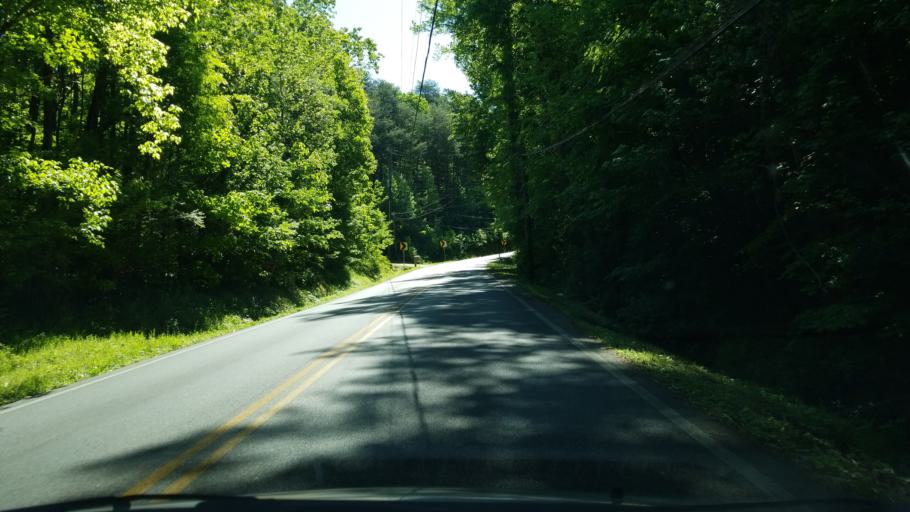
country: US
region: Tennessee
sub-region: Hamilton County
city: Falling Water
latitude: 35.1760
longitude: -85.2249
